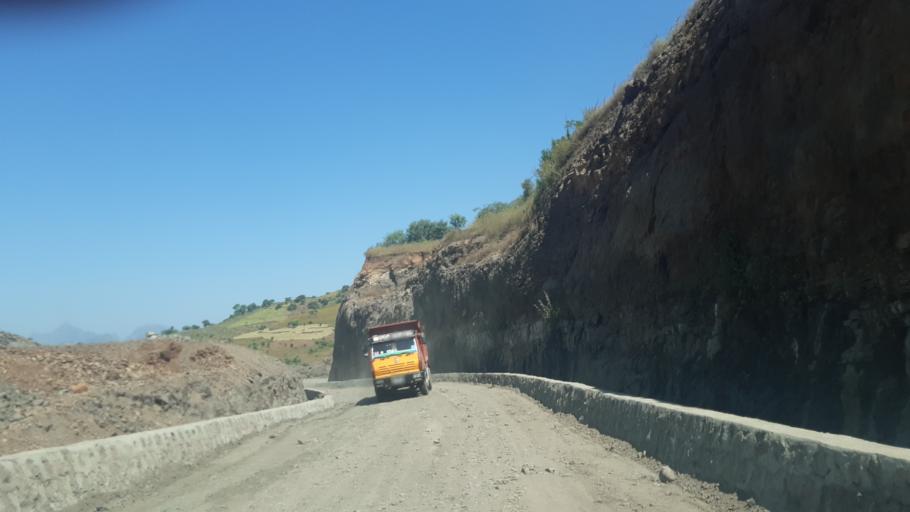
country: ET
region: Amhara
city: Dabat
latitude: 13.1654
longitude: 37.6057
